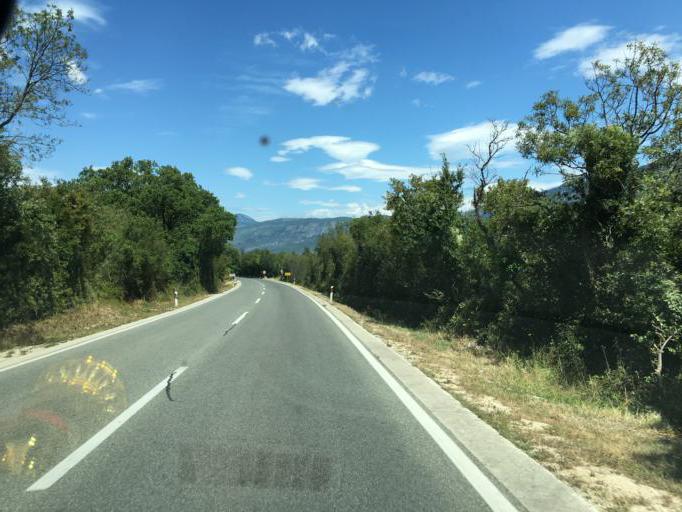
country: HR
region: Istarska
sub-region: Grad Labin
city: Labin
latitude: 45.1404
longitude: 14.1473
